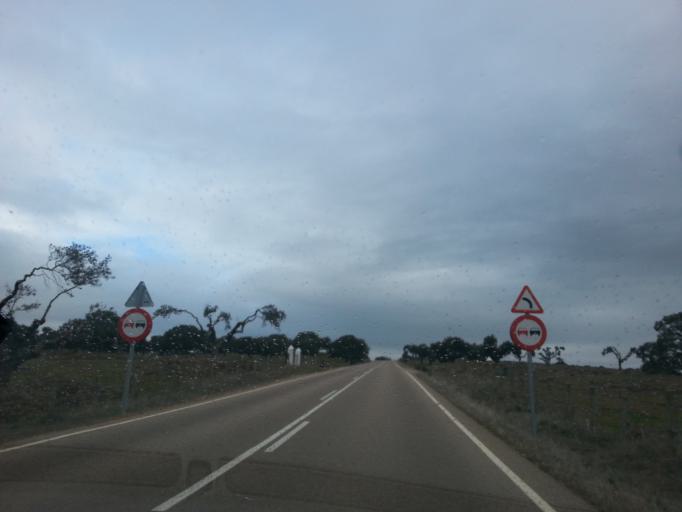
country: ES
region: Castille and Leon
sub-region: Provincia de Salamanca
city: Berrocal de Huebra
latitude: 40.7043
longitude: -6.0122
